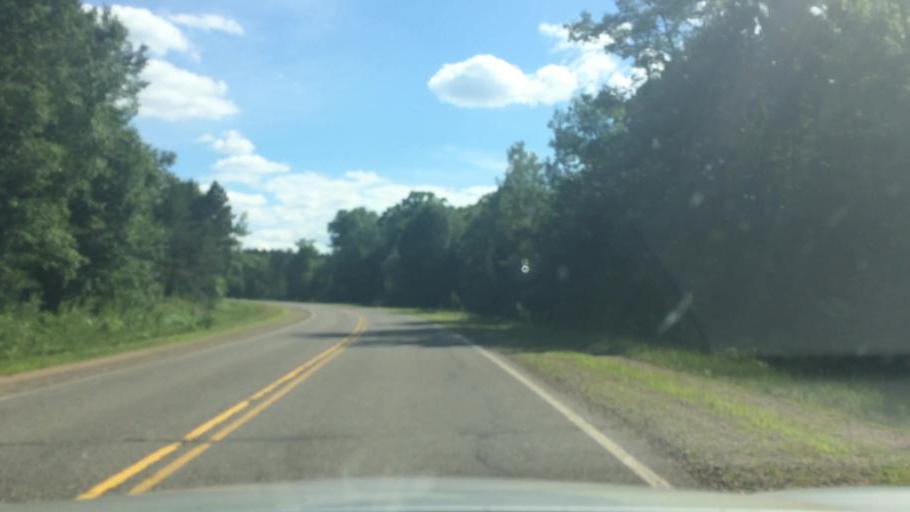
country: US
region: Wisconsin
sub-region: Vilas County
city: Lac du Flambeau
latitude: 46.0594
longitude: -89.6493
